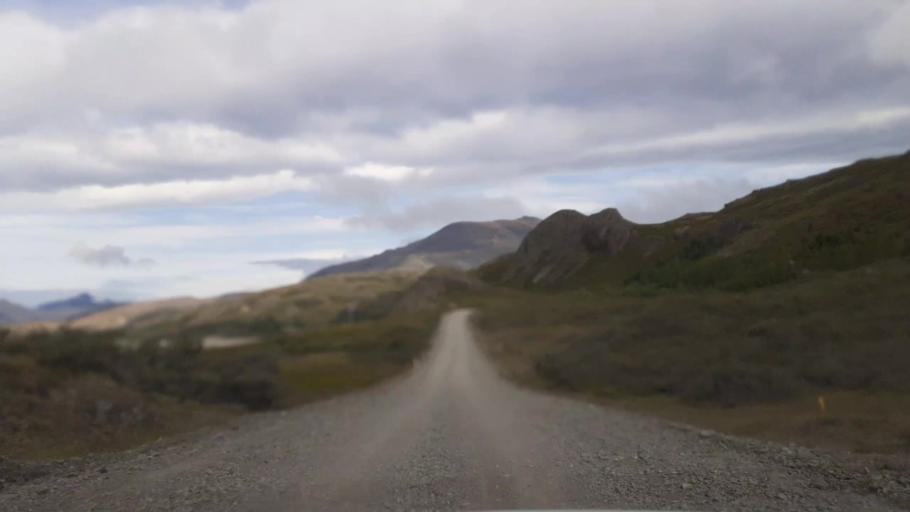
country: IS
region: East
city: Hoefn
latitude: 64.4272
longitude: -14.8840
